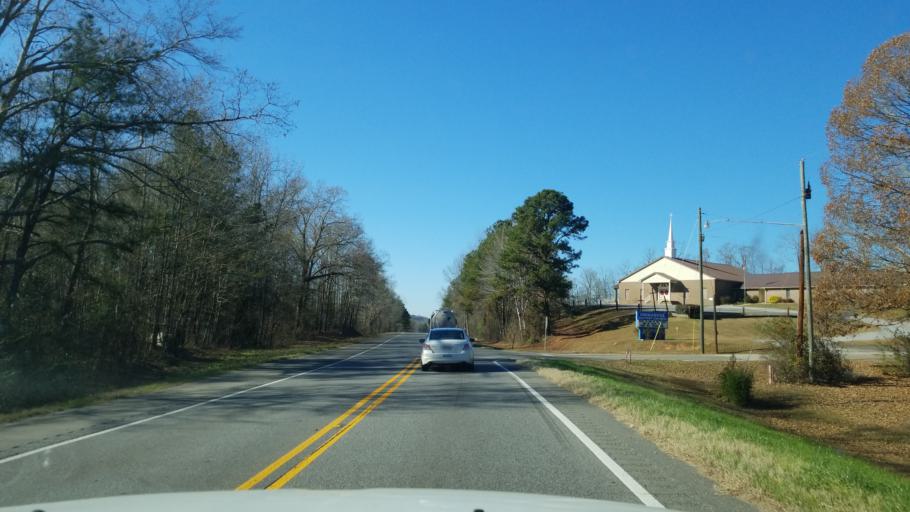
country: US
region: Alabama
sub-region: Pickens County
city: Gordo
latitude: 33.3319
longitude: -87.9158
